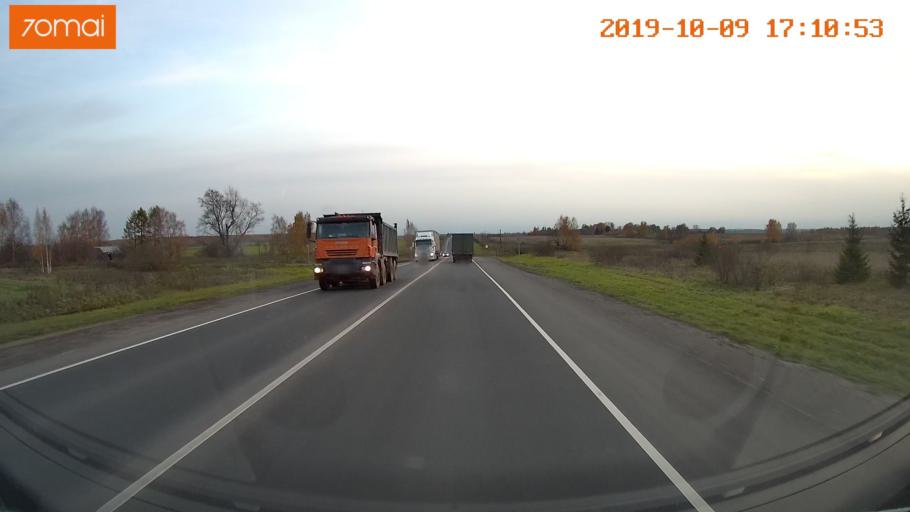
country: RU
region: Ivanovo
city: Privolzhsk
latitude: 57.3498
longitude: 41.2540
